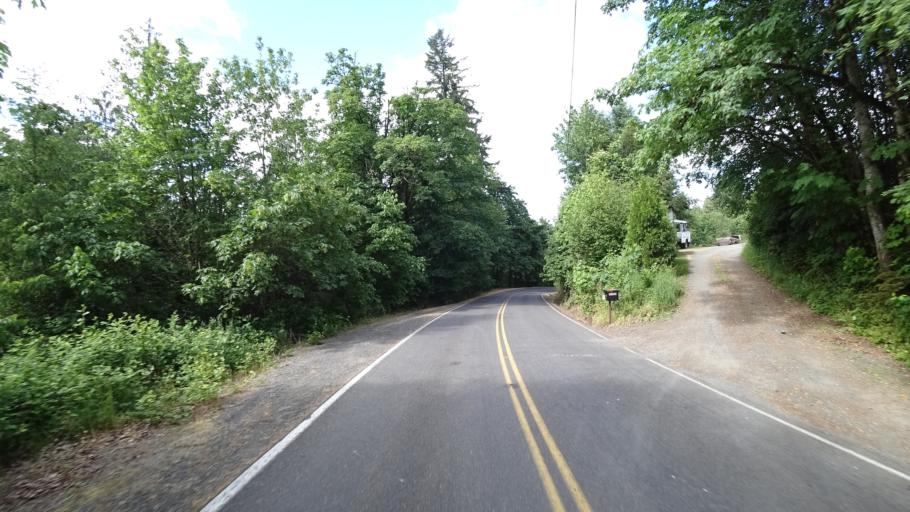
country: US
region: Oregon
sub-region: Washington County
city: Bethany
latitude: 45.6132
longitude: -122.8181
